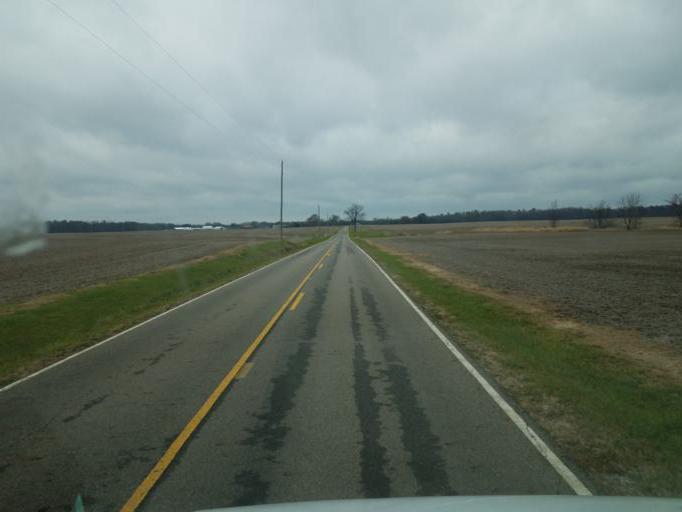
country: US
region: Ohio
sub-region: Licking County
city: Johnstown
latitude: 40.2231
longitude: -82.6308
